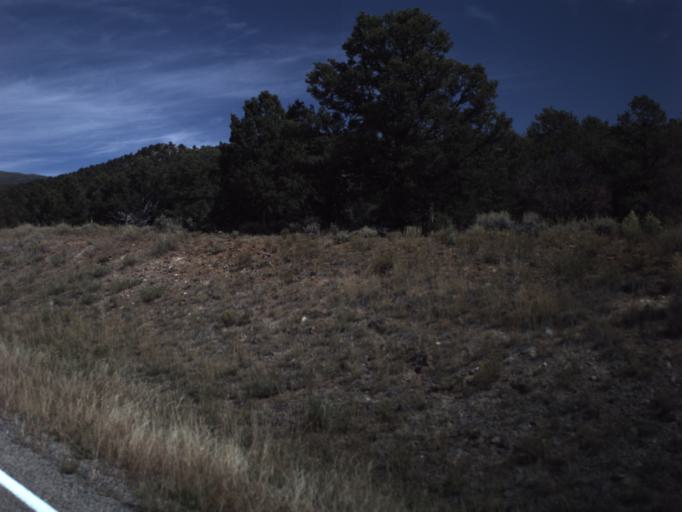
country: US
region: Utah
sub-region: Wayne County
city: Loa
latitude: 37.9606
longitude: -111.4348
